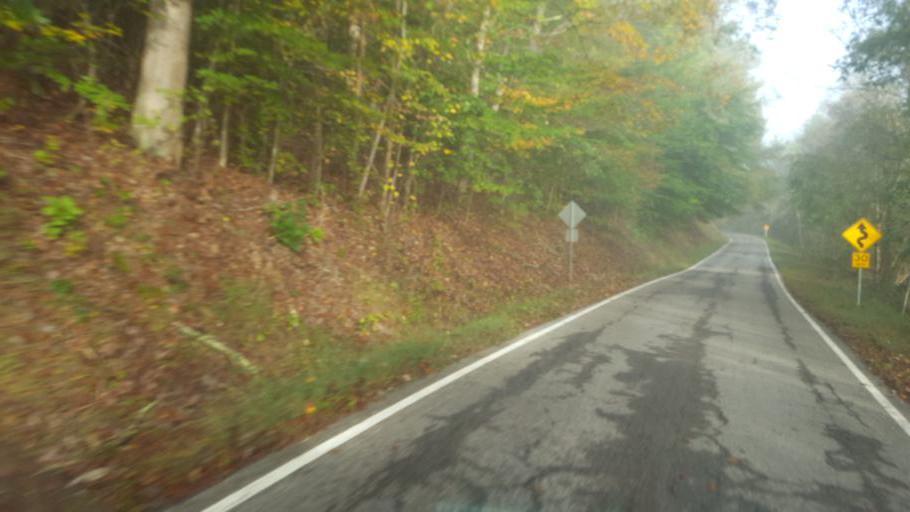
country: US
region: Ohio
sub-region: Adams County
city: Manchester
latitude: 38.5129
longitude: -83.5066
